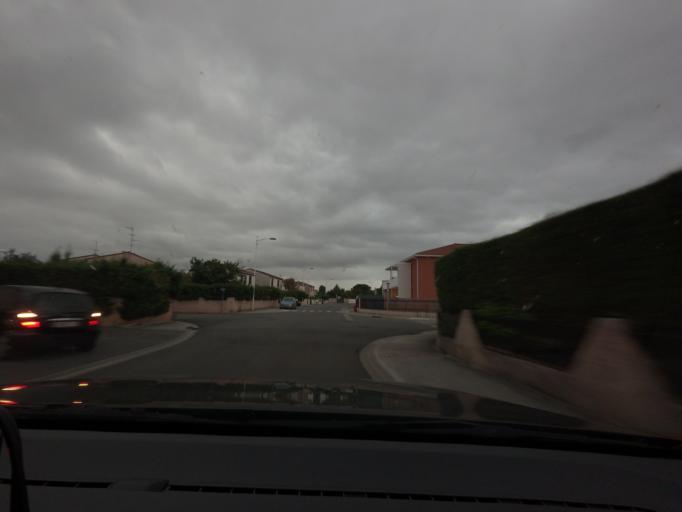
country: FR
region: Midi-Pyrenees
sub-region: Departement de la Haute-Garonne
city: Tournefeuille
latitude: 43.5868
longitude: 1.3413
